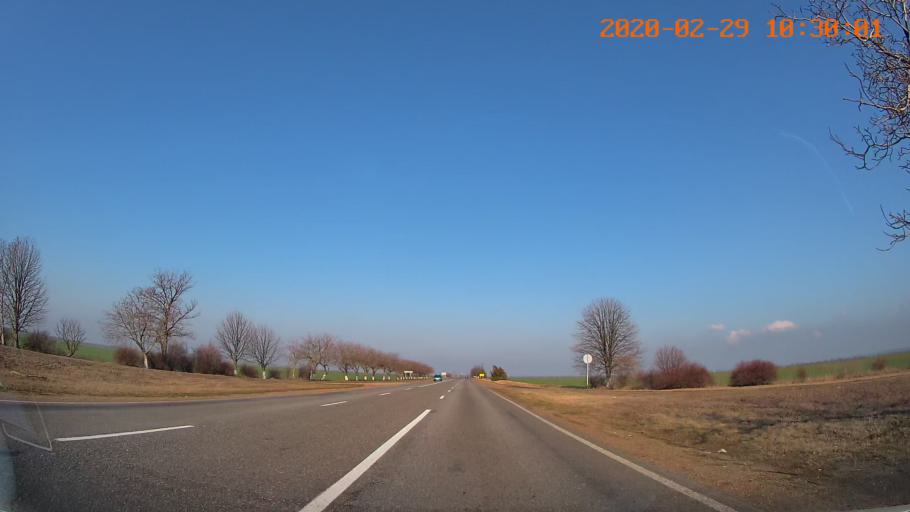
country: MD
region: Telenesti
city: Tiraspolul Nou
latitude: 46.9301
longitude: 29.5800
